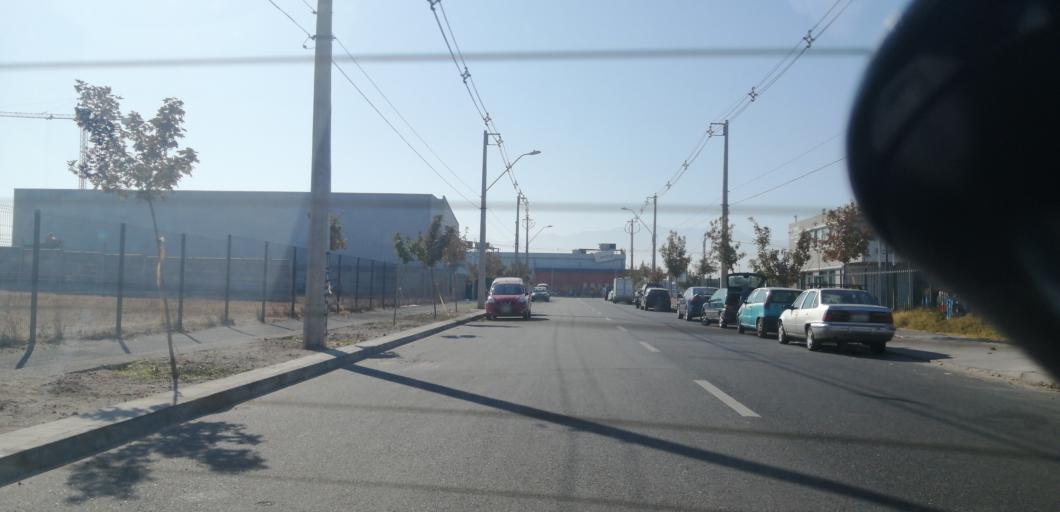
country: CL
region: Santiago Metropolitan
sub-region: Provincia de Santiago
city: Lo Prado
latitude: -33.4431
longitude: -70.7769
